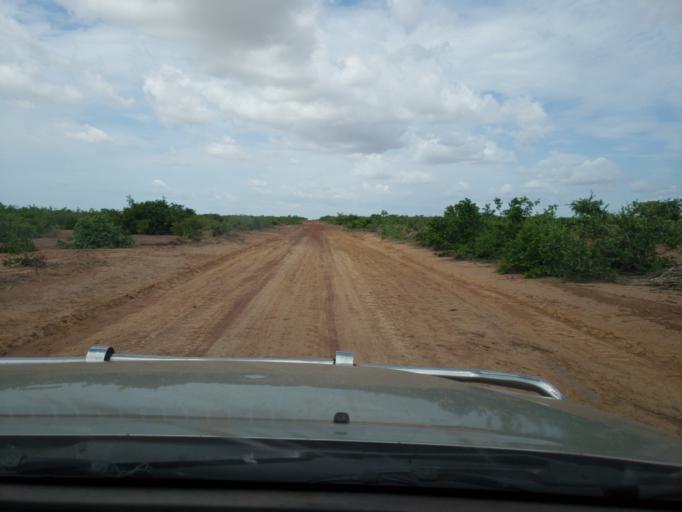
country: ML
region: Segou
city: Bla
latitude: 12.7082
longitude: -5.6996
